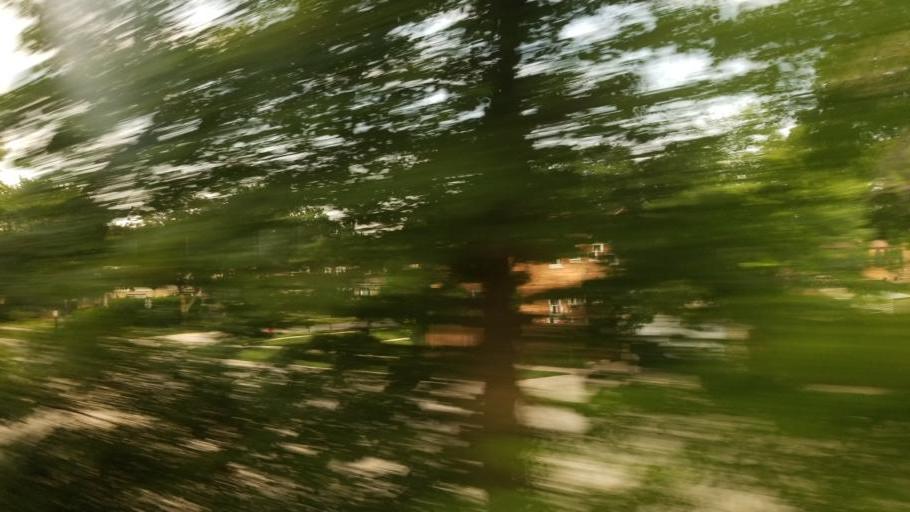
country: US
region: Illinois
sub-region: Cook County
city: Western Springs
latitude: 41.8105
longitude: -87.8953
